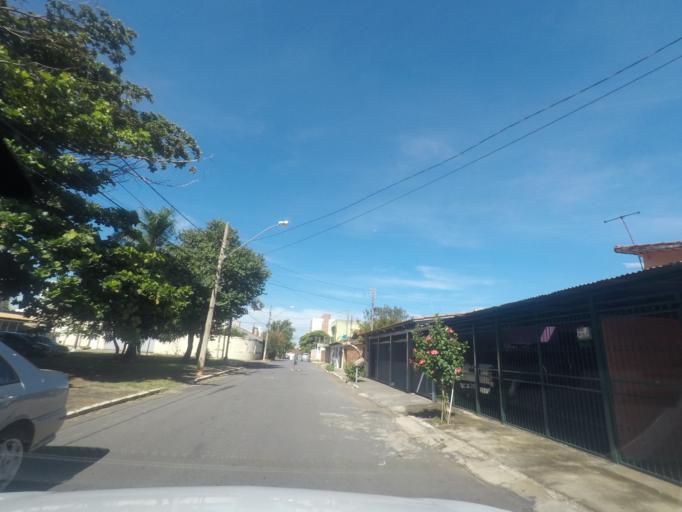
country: BR
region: Goias
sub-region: Goiania
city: Goiania
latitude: -16.6660
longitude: -49.2641
